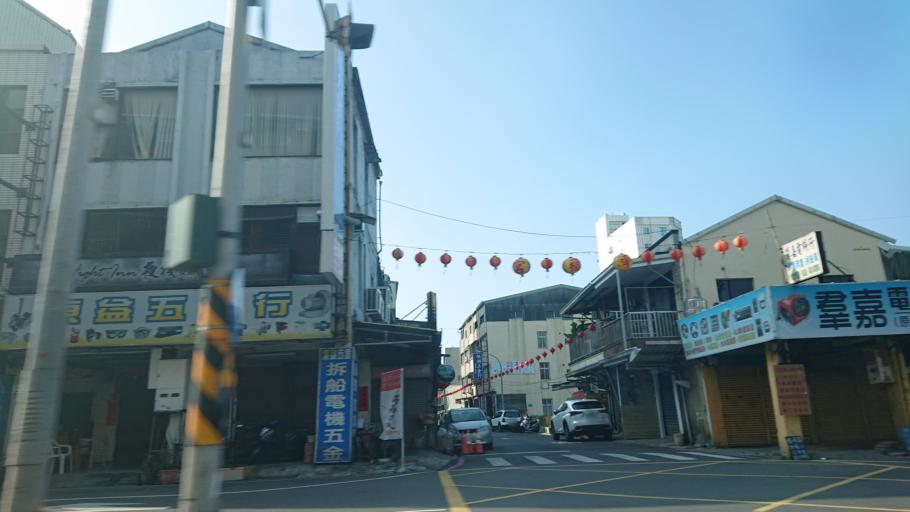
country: TW
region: Taiwan
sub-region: Tainan
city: Tainan
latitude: 22.9963
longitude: 120.1935
